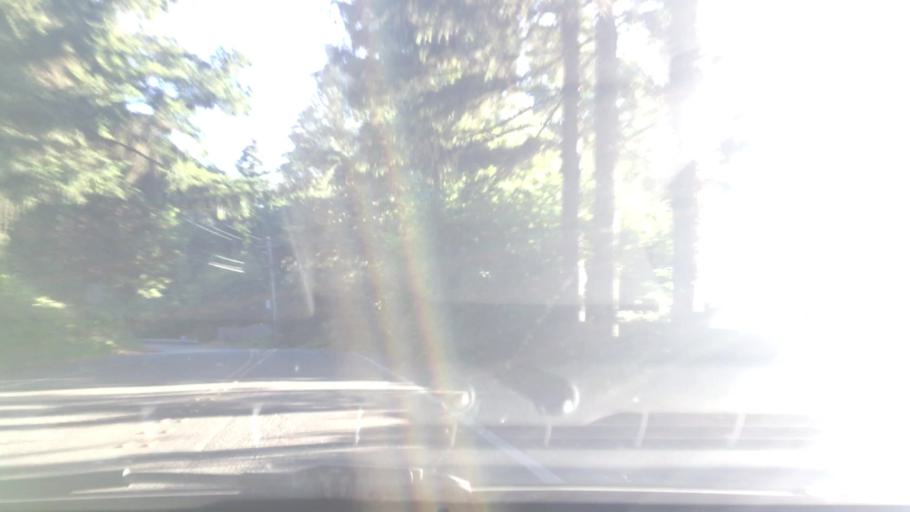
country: US
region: Washington
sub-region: King County
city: Sammamish
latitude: 47.6157
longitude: -122.1073
